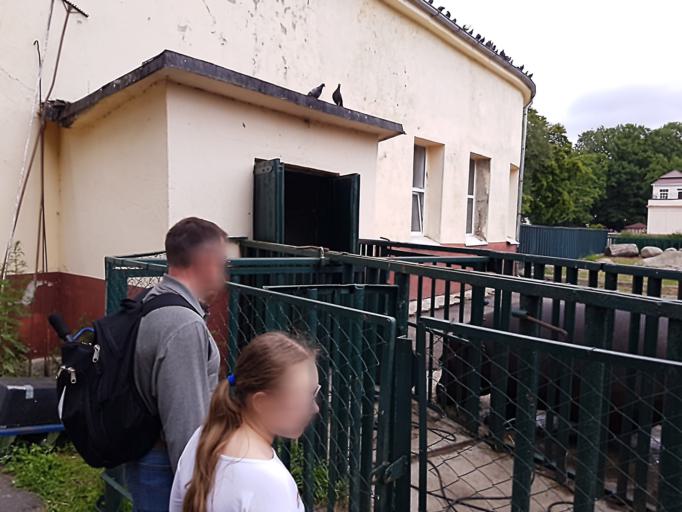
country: RU
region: Kaliningrad
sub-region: Gorod Kaliningrad
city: Kaliningrad
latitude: 54.7221
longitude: 20.4853
